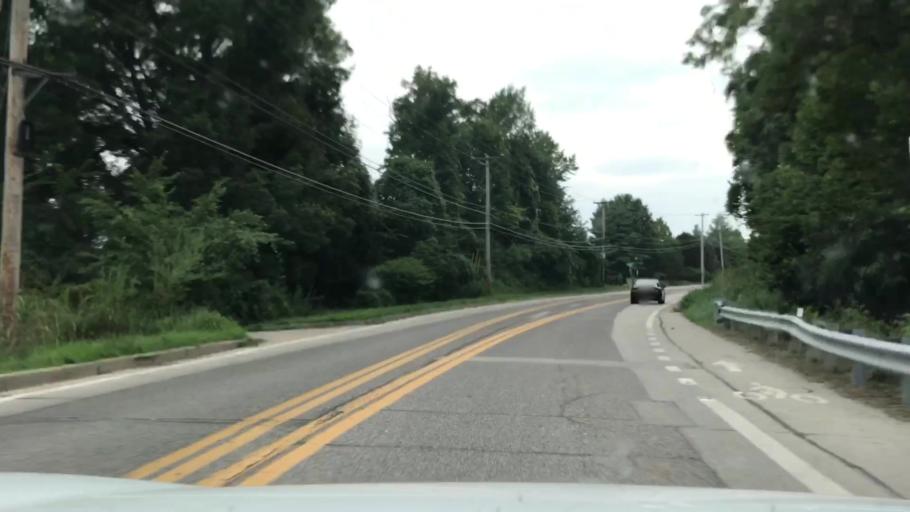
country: US
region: Missouri
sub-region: Saint Louis County
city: Chesterfield
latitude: 38.6541
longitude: -90.5968
